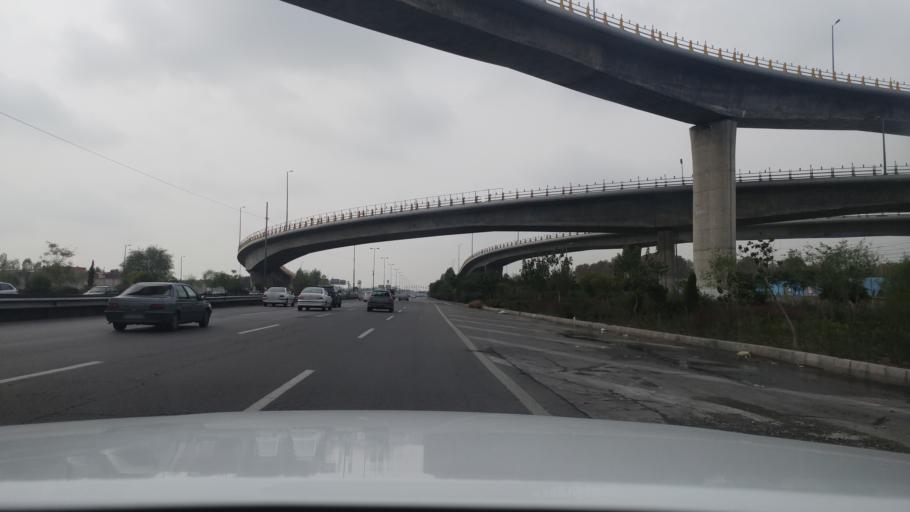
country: IR
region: Tehran
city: Tehran
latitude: 35.7168
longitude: 51.2991
